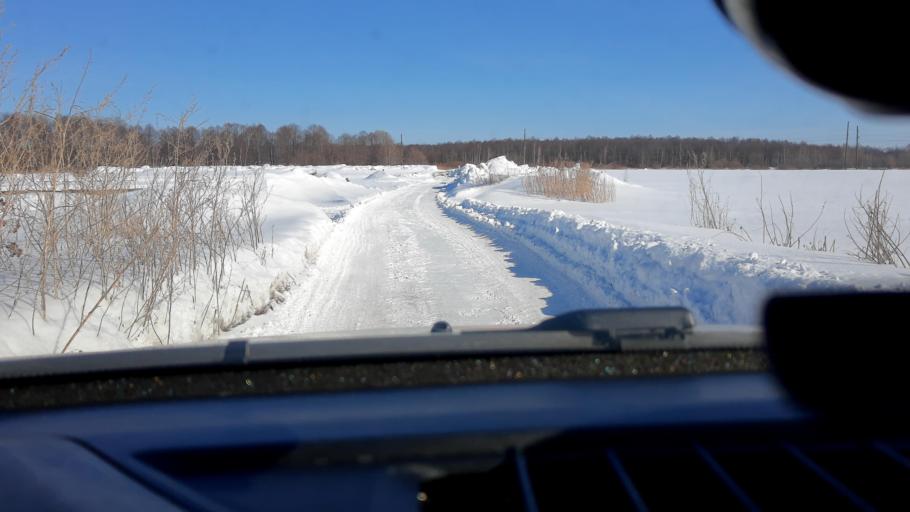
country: RU
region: Nizjnij Novgorod
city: Volodarsk
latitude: 56.2463
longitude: 43.1982
